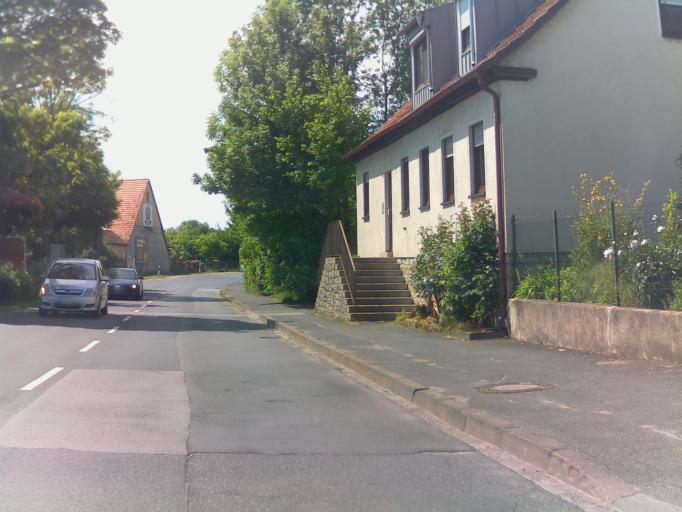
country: DE
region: Bavaria
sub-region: Regierungsbezirk Unterfranken
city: Arnstein
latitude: 49.9782
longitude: 9.9632
